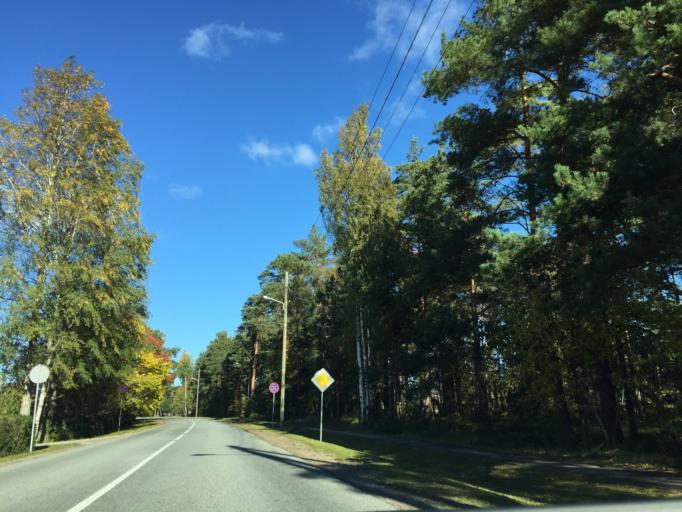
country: LV
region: Mesraga
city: Mersrags
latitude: 57.2489
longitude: 23.1738
